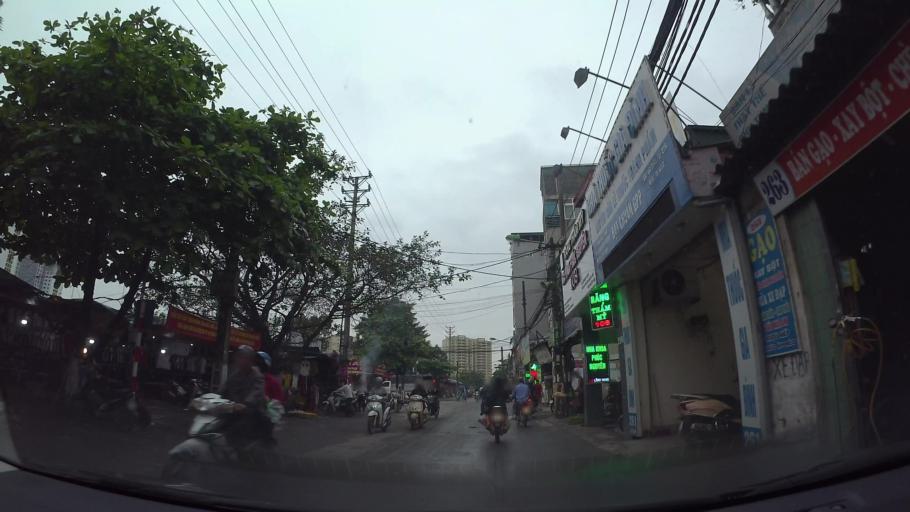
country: VN
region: Ha Noi
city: Hai BaTrung
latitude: 20.9843
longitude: 105.8739
